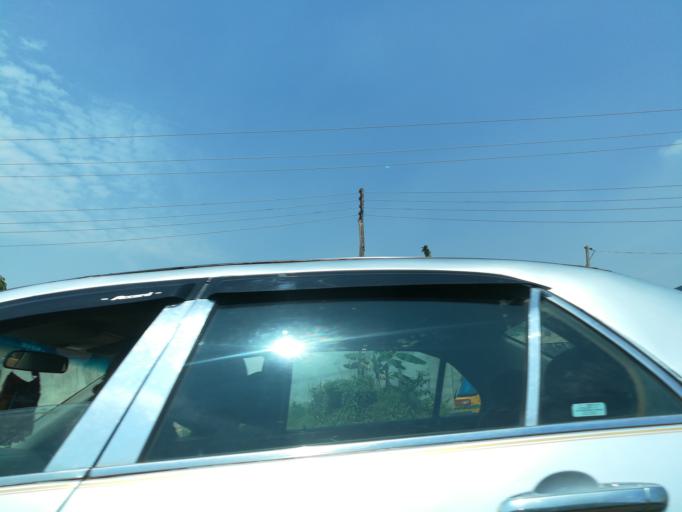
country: NG
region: Lagos
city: Ikorodu
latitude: 6.6552
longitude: 3.4764
